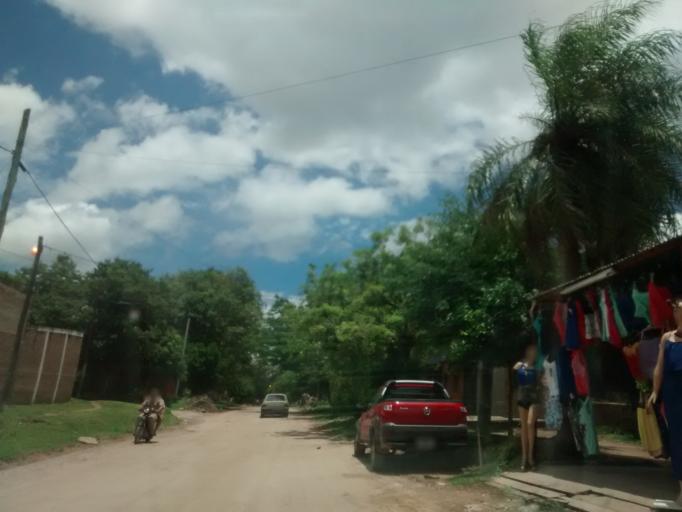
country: AR
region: Chaco
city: Fontana
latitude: -27.4302
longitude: -59.0000
